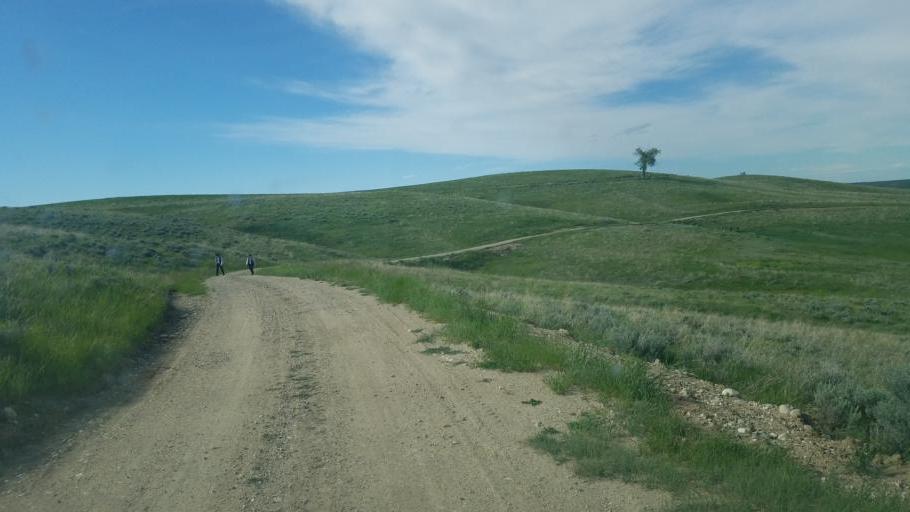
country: US
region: Montana
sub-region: Carbon County
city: Red Lodge
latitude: 45.3692
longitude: -109.1898
